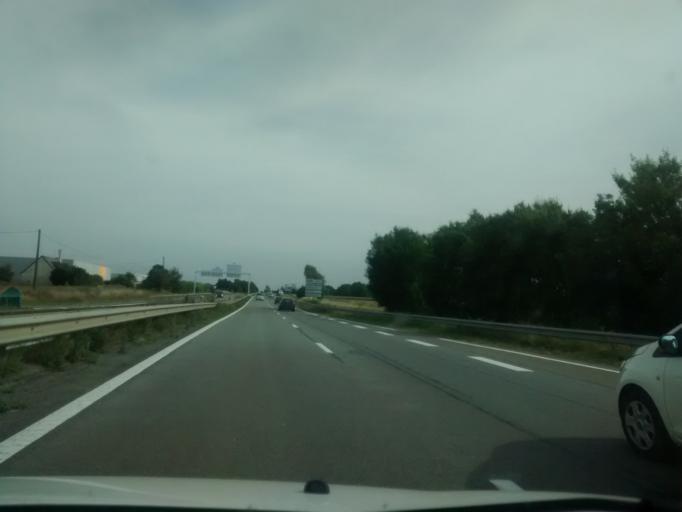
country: FR
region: Brittany
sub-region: Departement d'Ille-et-Vilaine
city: Miniac-Morvan
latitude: 48.5407
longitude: -1.9204
